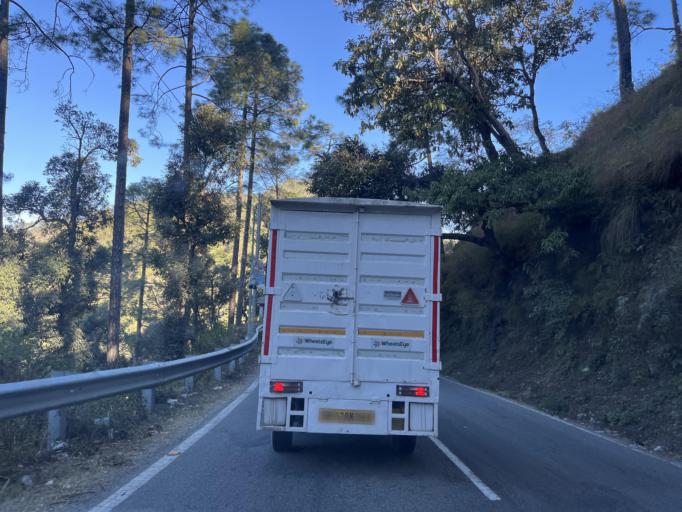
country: IN
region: Uttarakhand
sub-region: Naini Tal
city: Bhowali
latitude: 29.4004
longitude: 79.5087
